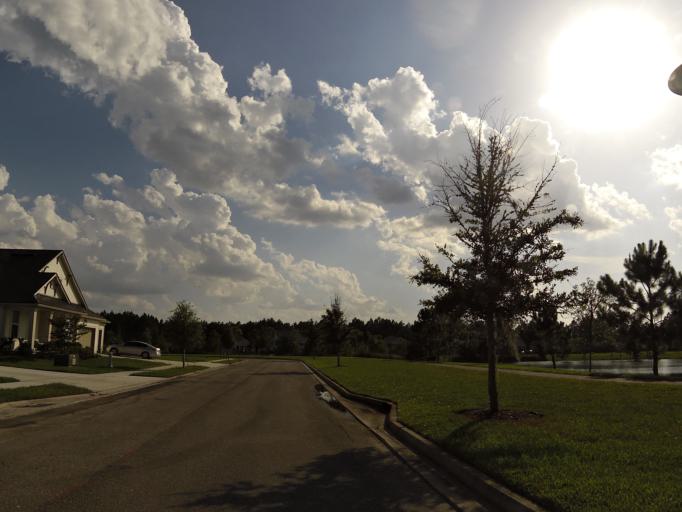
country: US
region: Florida
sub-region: Clay County
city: Green Cove Springs
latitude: 30.0285
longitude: -81.6331
